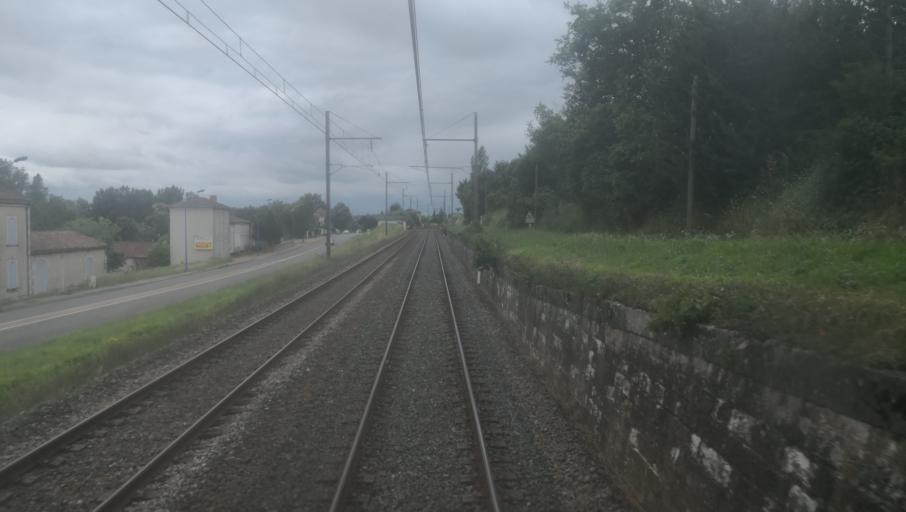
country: FR
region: Aquitaine
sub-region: Departement du Lot-et-Garonne
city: Sainte-Colombe-en-Bruilhois
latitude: 44.2402
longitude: 0.4810
